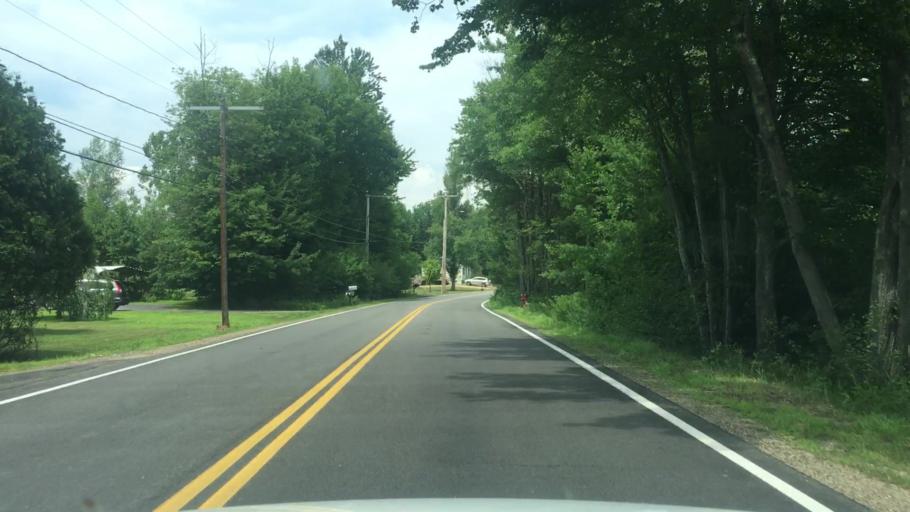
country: US
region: New Hampshire
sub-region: Strafford County
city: Rochester
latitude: 43.3359
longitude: -70.9584
